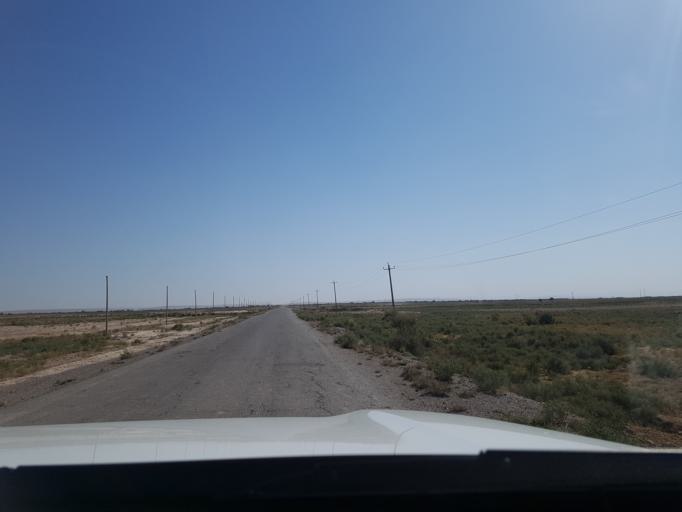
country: IR
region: Razavi Khorasan
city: Sarakhs
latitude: 36.5075
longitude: 61.2533
